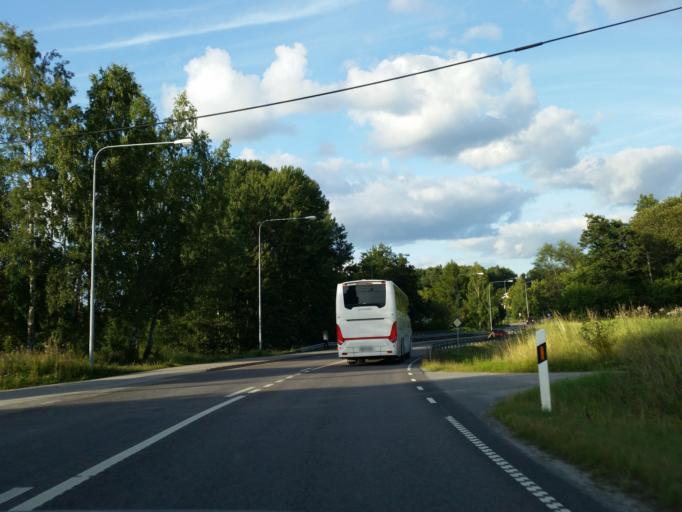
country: SE
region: Stockholm
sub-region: Sodertalje Kommun
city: Pershagen
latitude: 59.0823
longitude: 17.5506
